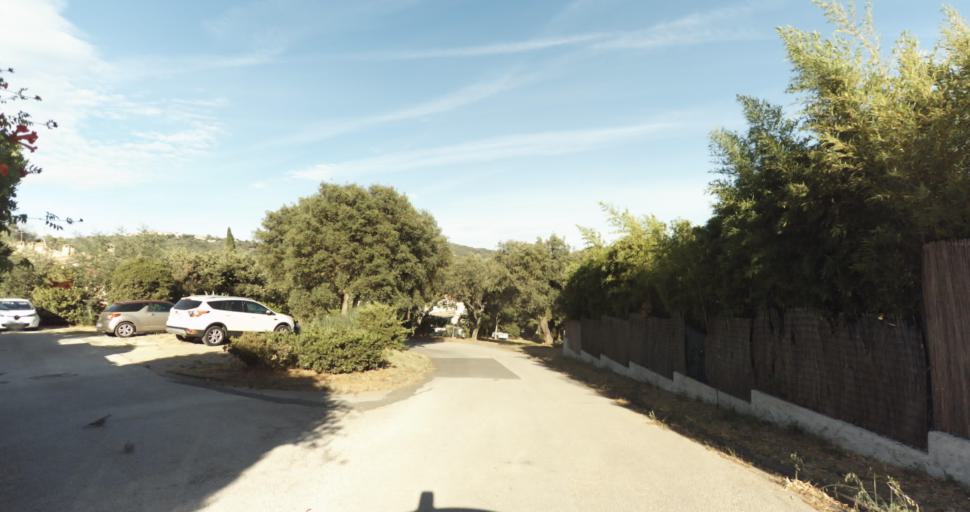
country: FR
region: Provence-Alpes-Cote d'Azur
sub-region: Departement du Var
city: La Croix-Valmer
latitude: 43.2240
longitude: 6.5660
